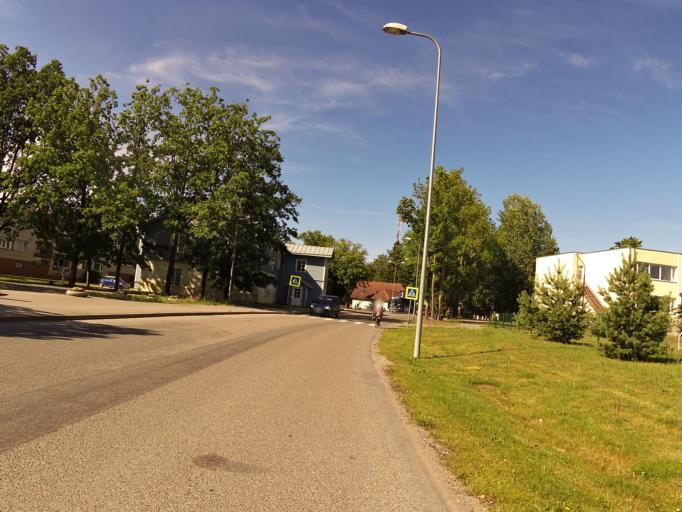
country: EE
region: Hiiumaa
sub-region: Kaerdla linn
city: Kardla
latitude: 59.0005
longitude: 22.7464
